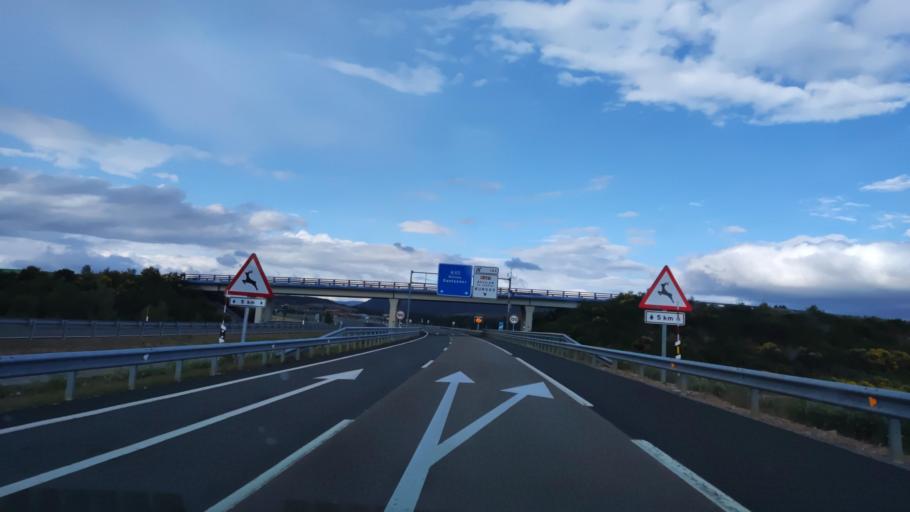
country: ES
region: Castille and Leon
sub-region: Provincia de Palencia
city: Aguilar de Campoo
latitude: 42.7737
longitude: -4.2487
